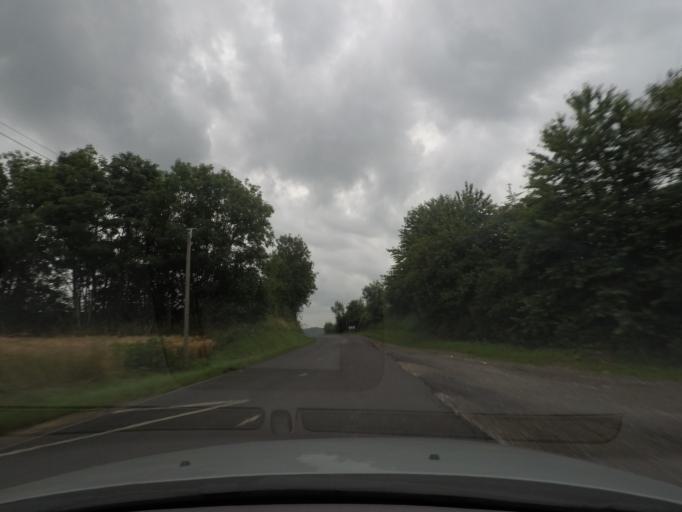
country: FR
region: Haute-Normandie
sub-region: Departement de la Seine-Maritime
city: Neufchatel-en-Bray
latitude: 49.7291
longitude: 1.4633
